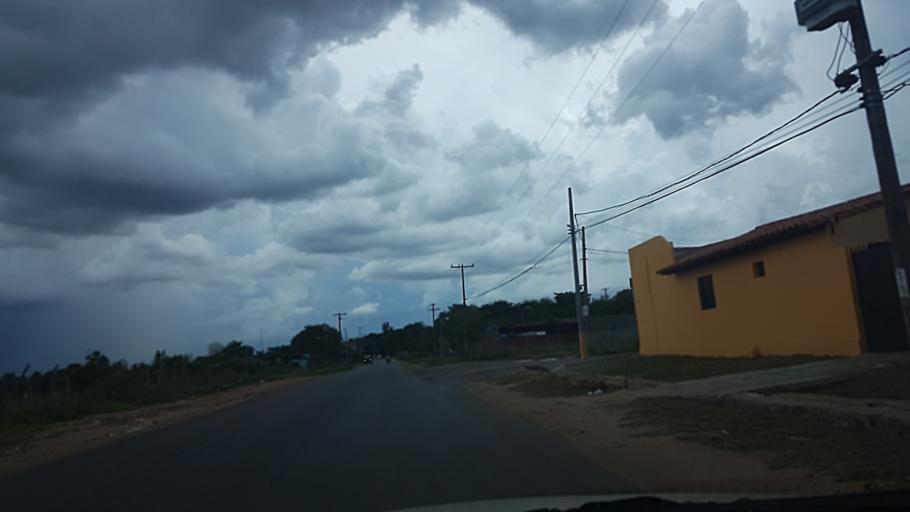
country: PY
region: Central
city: Limpio
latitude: -25.2131
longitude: -57.5145
